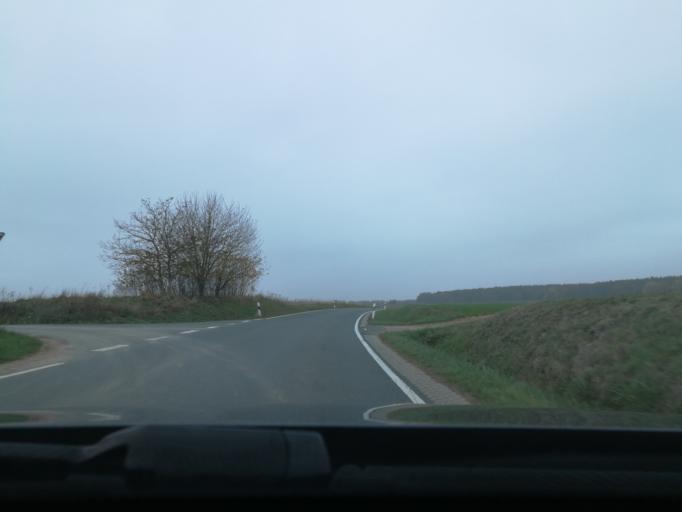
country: DE
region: Bavaria
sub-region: Regierungsbezirk Mittelfranken
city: Tuchenbach
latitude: 49.5351
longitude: 10.8525
